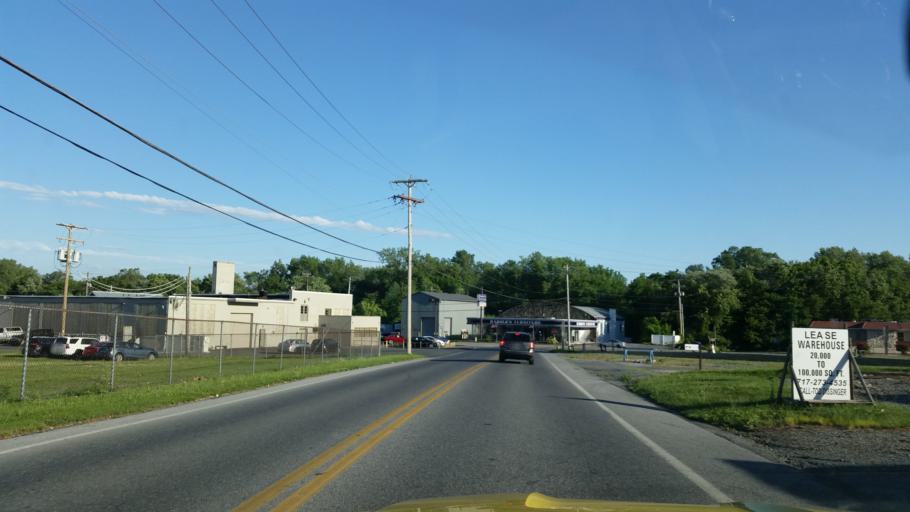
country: US
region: Pennsylvania
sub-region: Lebanon County
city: Pleasant Hill
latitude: 40.3407
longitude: -76.4563
